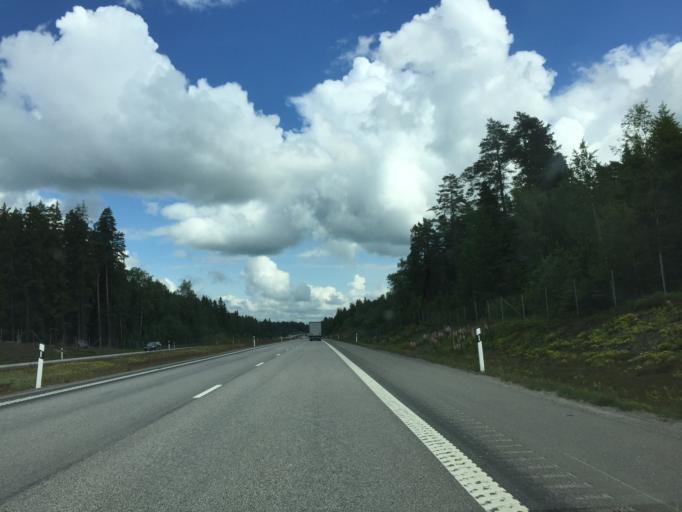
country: SE
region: OErebro
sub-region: Lindesbergs Kommun
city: Fellingsbro
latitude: 59.3565
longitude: 15.5653
